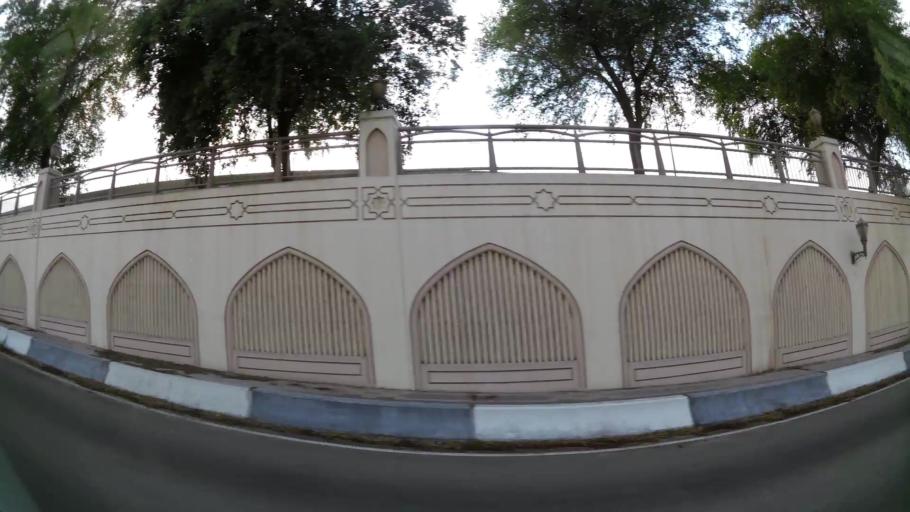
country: AE
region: Abu Dhabi
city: Abu Dhabi
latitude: 24.3732
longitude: 54.5276
